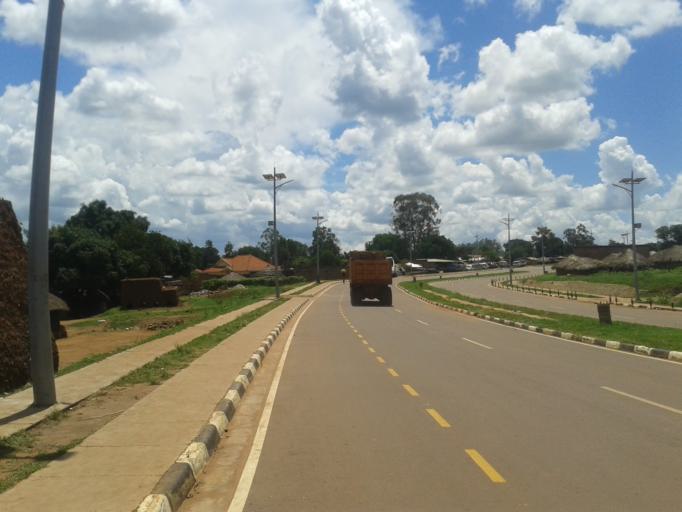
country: UG
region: Northern Region
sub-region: Gulu District
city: Gulu
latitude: 2.7638
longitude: 32.2941
